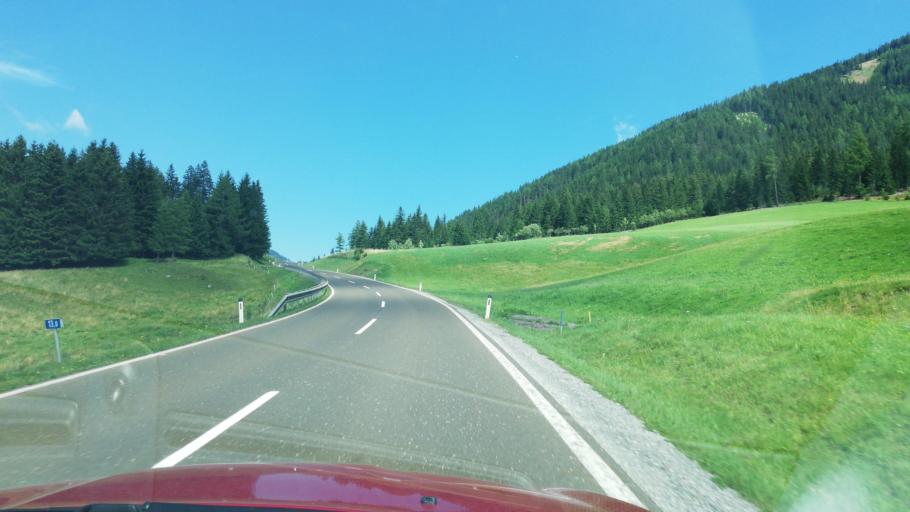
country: AT
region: Styria
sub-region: Politischer Bezirk Murtal
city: Hohentauern
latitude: 47.4070
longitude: 14.4643
